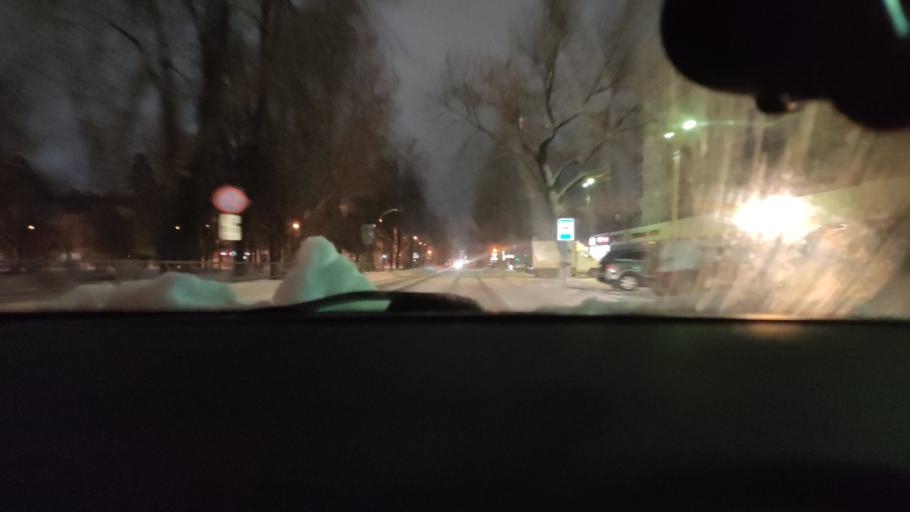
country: RU
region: Perm
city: Krasnokamsk
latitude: 58.0827
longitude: 55.7472
